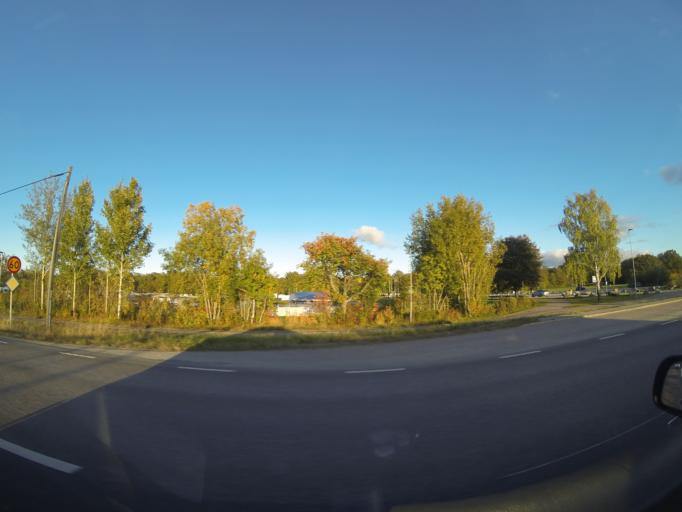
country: SE
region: Vaestmanland
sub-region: Vasteras
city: Vasteras
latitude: 59.5745
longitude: 16.5193
